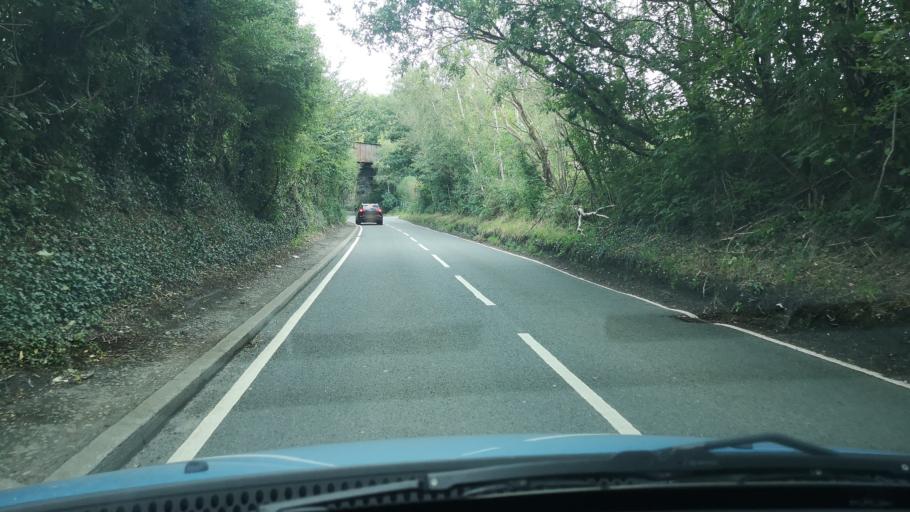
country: GB
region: England
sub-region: City and Borough of Wakefield
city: Horbury
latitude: 53.6430
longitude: -1.5502
